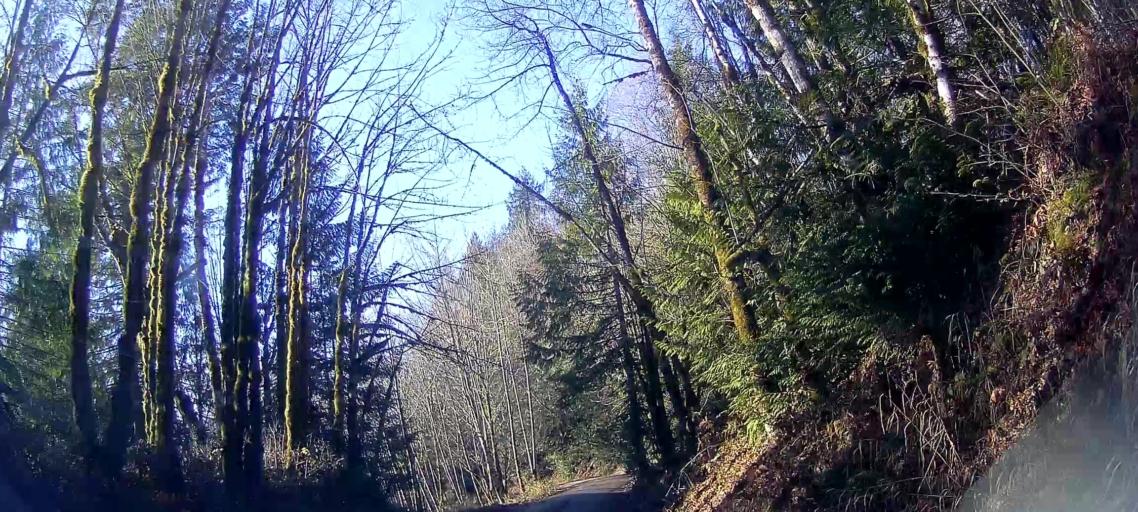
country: US
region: Washington
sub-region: Snohomish County
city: Darrington
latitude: 48.5410
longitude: -121.7340
